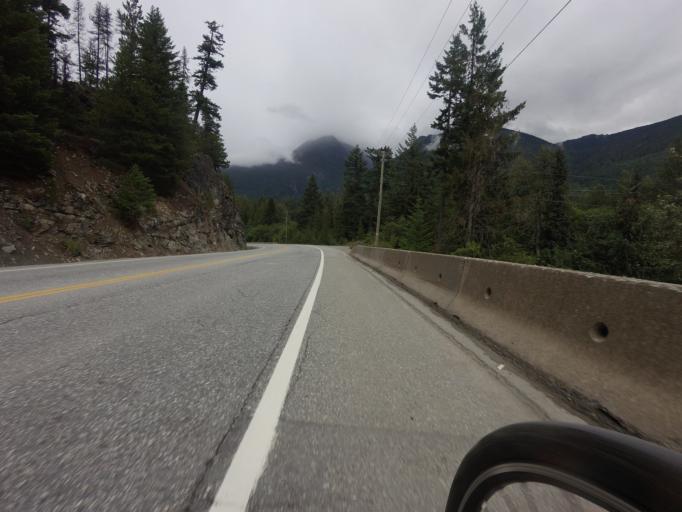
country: CA
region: British Columbia
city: Whistler
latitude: 50.1665
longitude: -122.8963
